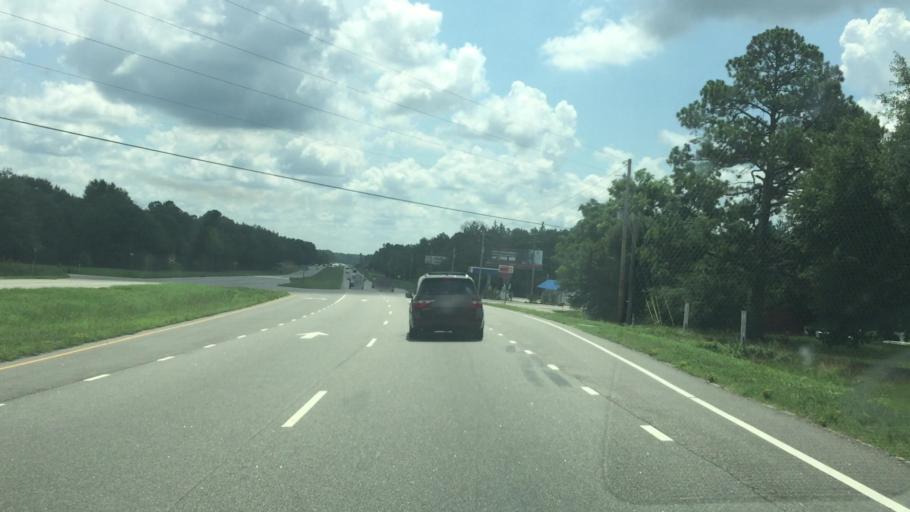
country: US
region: North Carolina
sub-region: Scotland County
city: Laurel Hill
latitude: 34.8282
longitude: -79.5926
